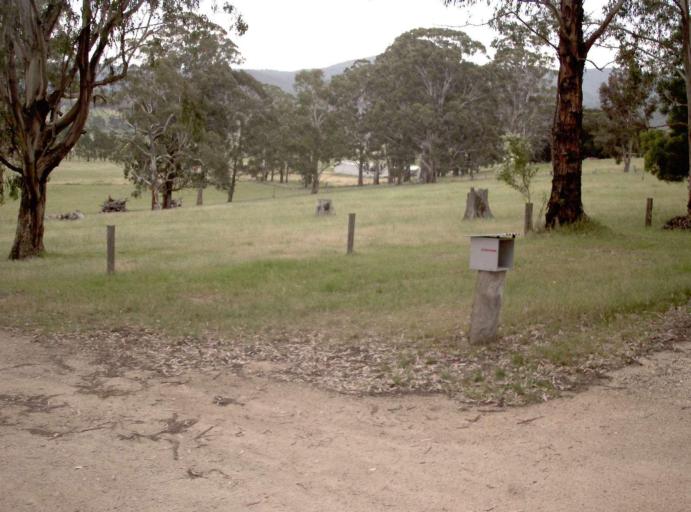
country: AU
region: New South Wales
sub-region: Bombala
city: Bombala
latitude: -37.4872
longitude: 149.1817
